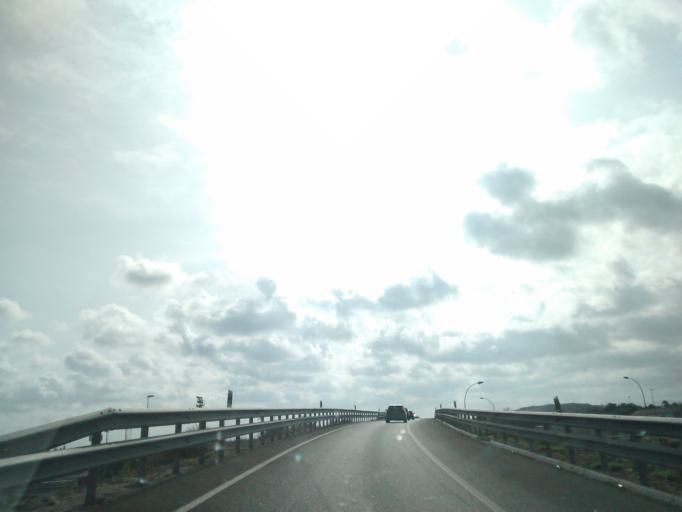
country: ES
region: Valencia
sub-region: Provincia de Alicante
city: el Campello
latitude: 38.4379
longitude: -0.4022
